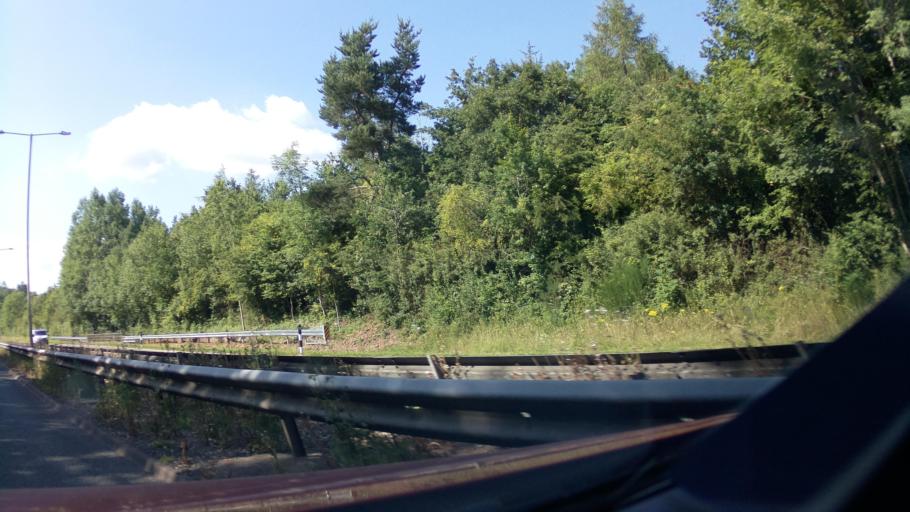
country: GB
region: England
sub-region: Worcestershire
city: Redditch
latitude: 52.3037
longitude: -1.9748
